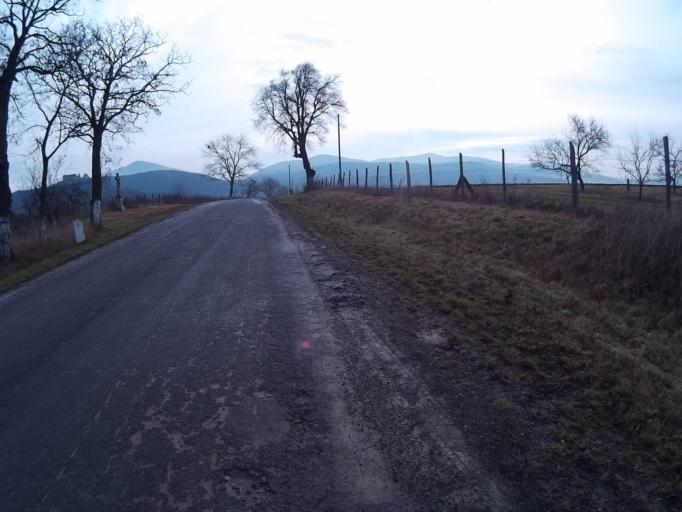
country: HU
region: Borsod-Abauj-Zemplen
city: Abaujszanto
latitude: 48.3416
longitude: 21.2194
